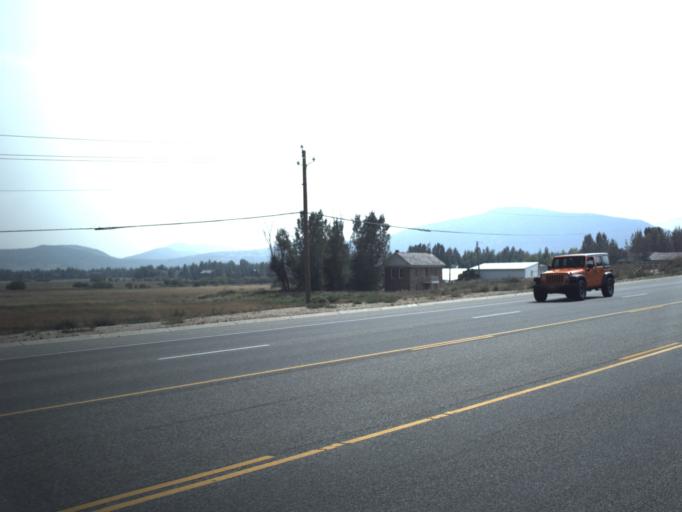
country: US
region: Utah
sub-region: Summit County
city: Snyderville
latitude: 40.7147
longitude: -111.5449
